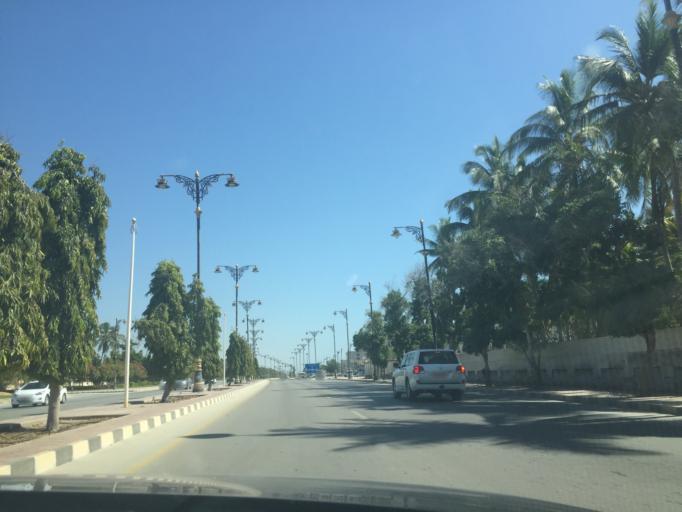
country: OM
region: Zufar
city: Salalah
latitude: 17.0261
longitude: 54.1547
